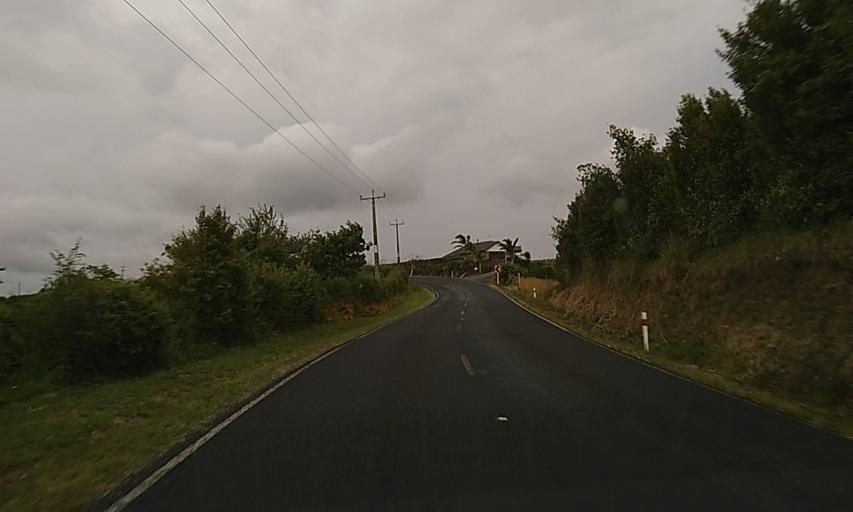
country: NZ
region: Auckland
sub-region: Auckland
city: Pukekohe East
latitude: -37.3208
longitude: 174.9247
